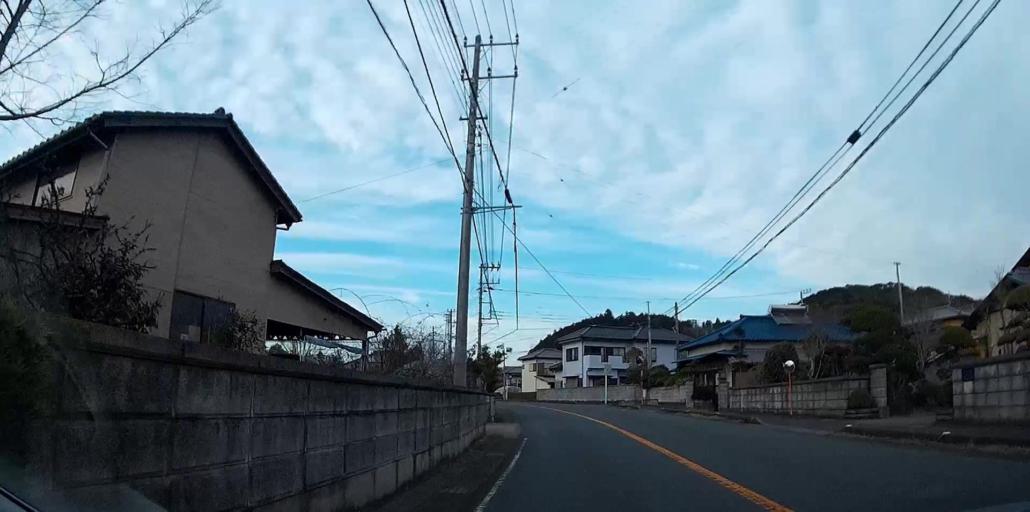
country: JP
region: Chiba
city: Kisarazu
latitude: 35.3760
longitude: 140.0623
